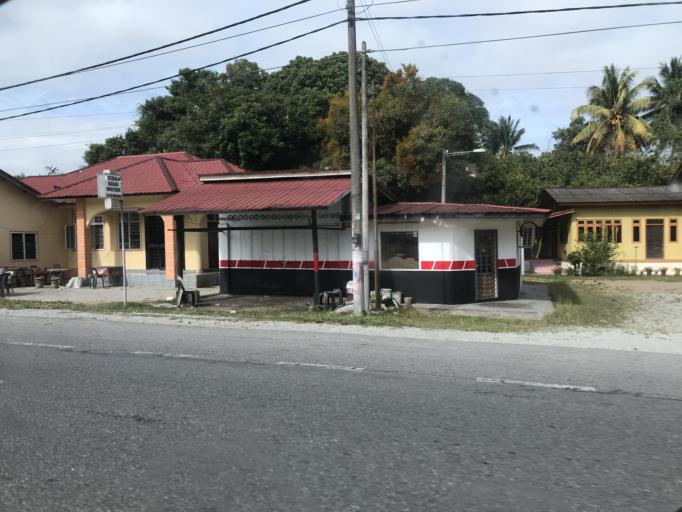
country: MY
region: Kelantan
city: Kota Bharu
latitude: 6.1289
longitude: 102.1791
